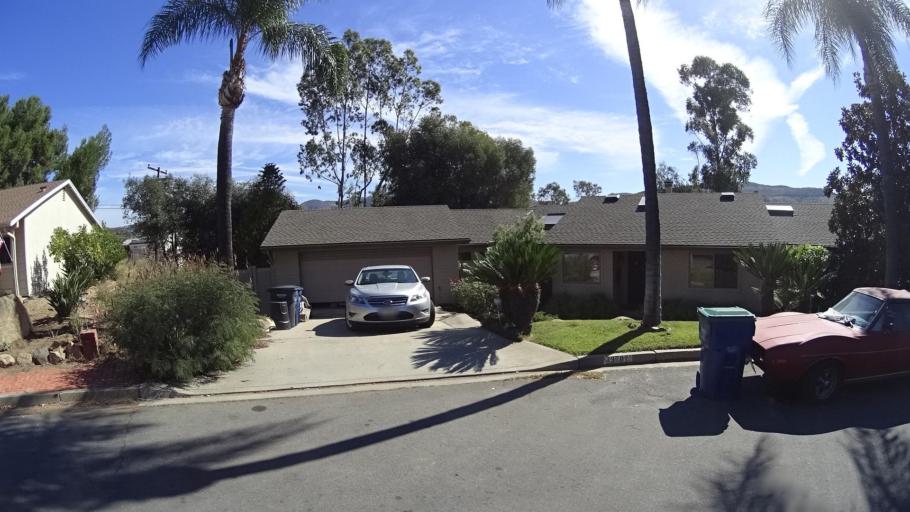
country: US
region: California
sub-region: San Diego County
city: Lakeside
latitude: 32.8432
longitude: -116.8937
